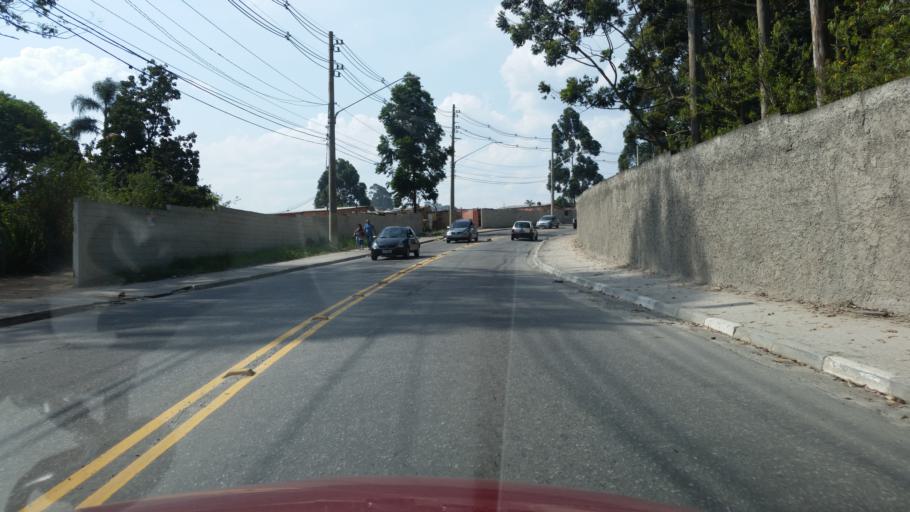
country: BR
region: Sao Paulo
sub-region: Ferraz De Vasconcelos
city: Ferraz de Vasconcelos
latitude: -23.5616
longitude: -46.4169
